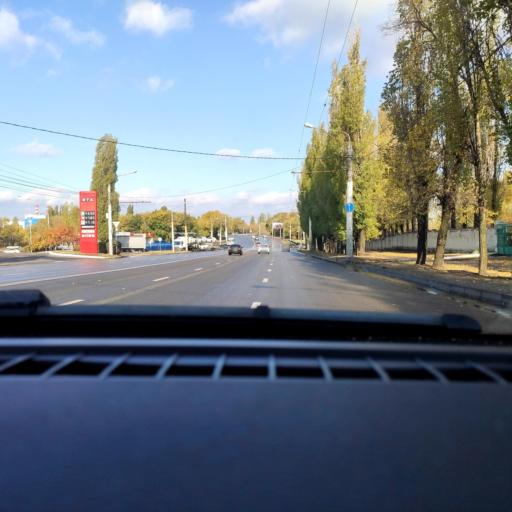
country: RU
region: Voronezj
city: Maslovka
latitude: 51.6197
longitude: 39.2365
